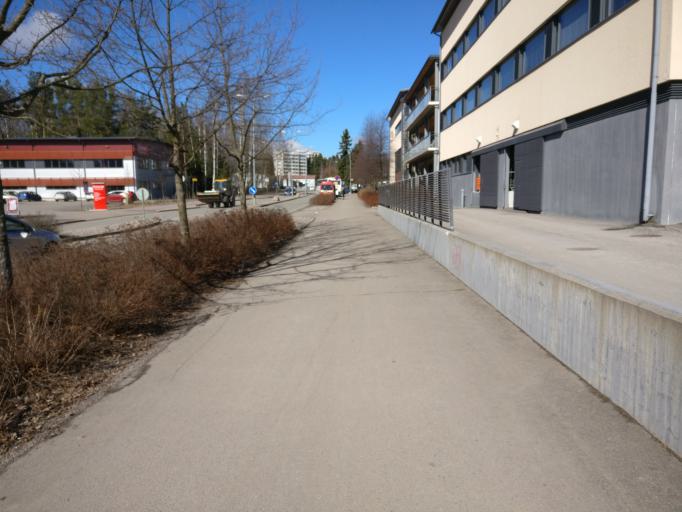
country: FI
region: Uusimaa
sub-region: Helsinki
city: Jaervenpaeae
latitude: 60.4802
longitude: 25.0819
